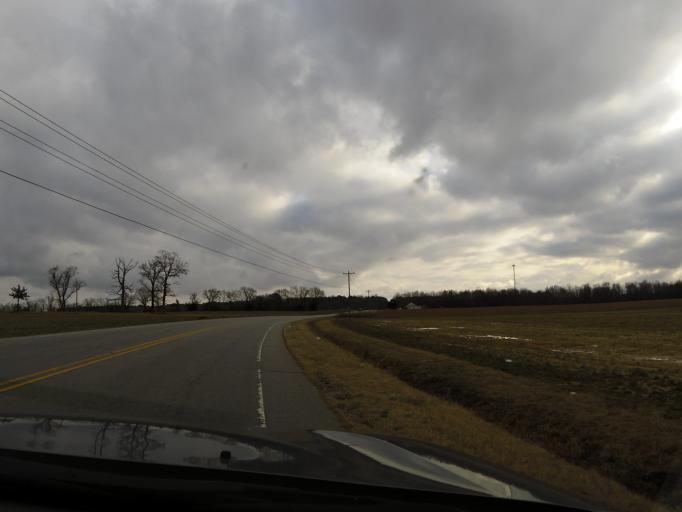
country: US
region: North Carolina
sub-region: Edgecombe County
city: Pinetops
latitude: 35.8483
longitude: -77.6635
